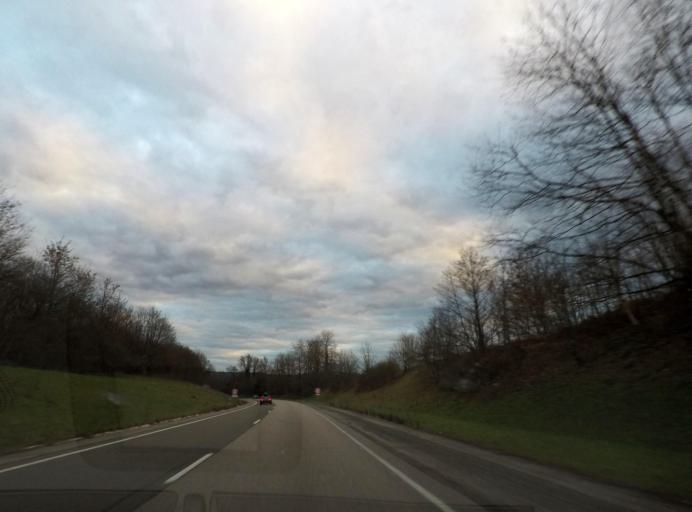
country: FR
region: Rhone-Alpes
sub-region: Departement de l'Ain
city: Saint-Martin-du-Mont
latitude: 46.0703
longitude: 5.3212
